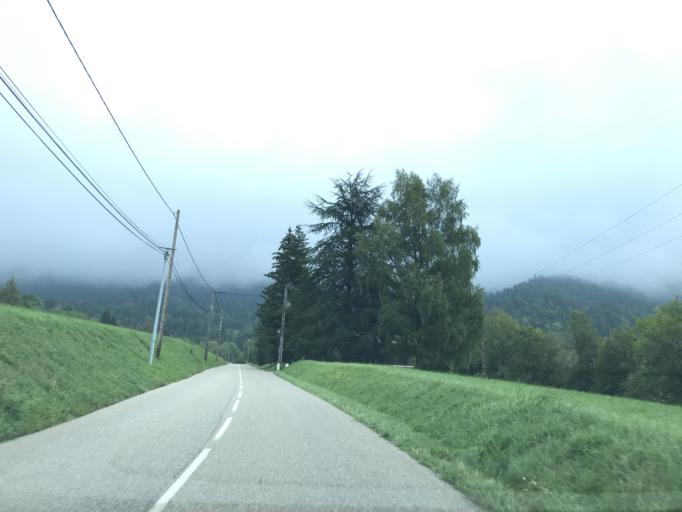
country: FR
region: Rhone-Alpes
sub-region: Departement de la Haute-Savoie
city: Talloires
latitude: 45.8347
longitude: 6.2337
